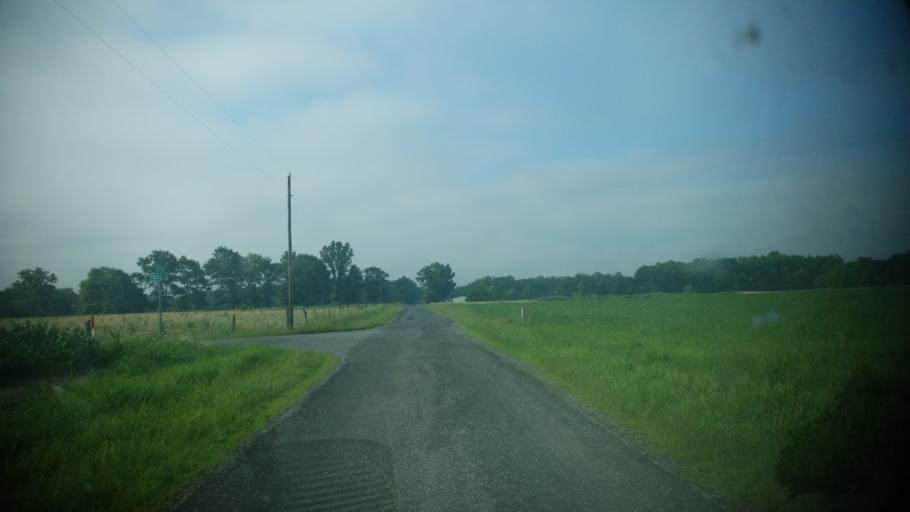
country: US
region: Illinois
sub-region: Clay County
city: Flora
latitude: 38.5809
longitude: -88.3646
